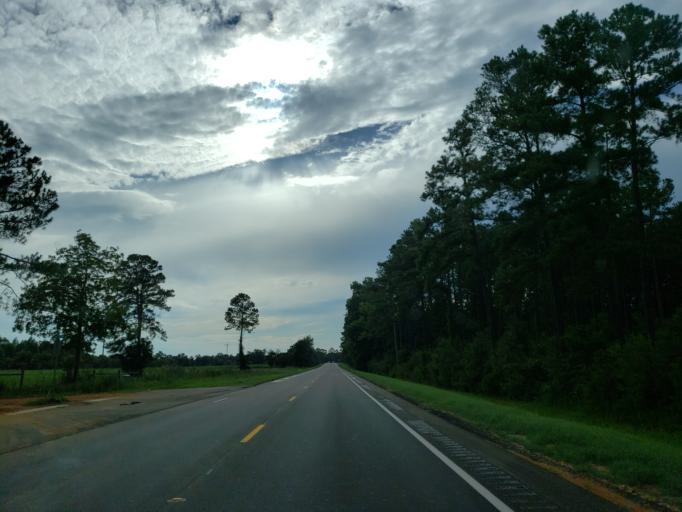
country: US
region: Georgia
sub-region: Irwin County
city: Ocilla
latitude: 31.5637
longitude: -83.3321
